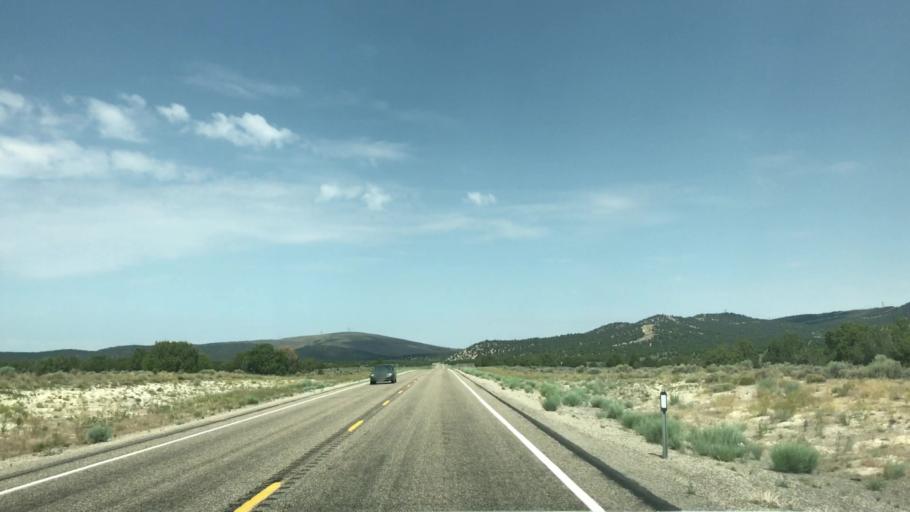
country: US
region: Nevada
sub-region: White Pine County
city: Ely
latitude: 39.3694
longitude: -115.0559
